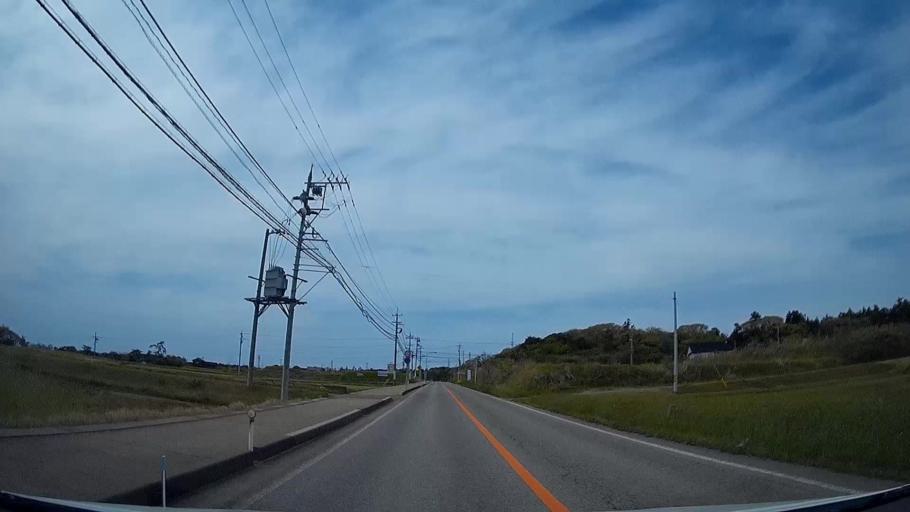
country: JP
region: Ishikawa
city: Hakui
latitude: 37.0469
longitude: 136.7376
